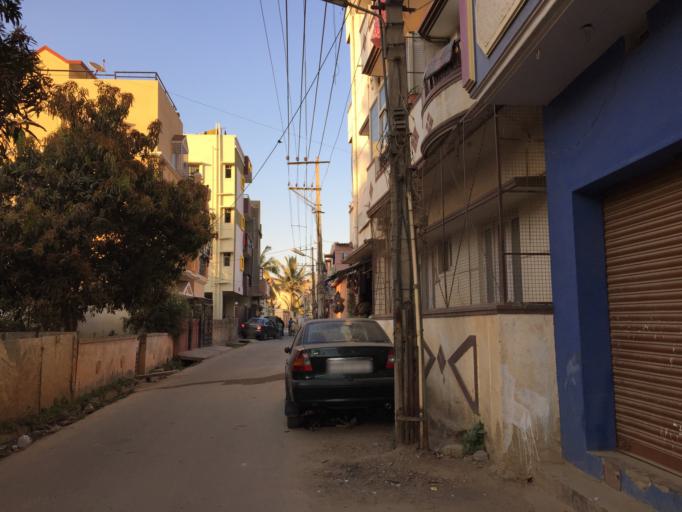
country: IN
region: Karnataka
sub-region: Bangalore Urban
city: Yelahanka
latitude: 13.0512
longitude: 77.6286
